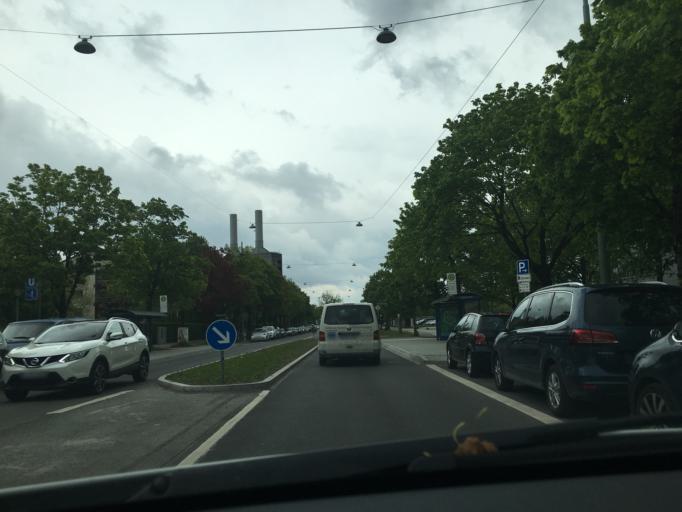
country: DE
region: Bavaria
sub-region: Upper Bavaria
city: Neuried
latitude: 48.0948
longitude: 11.5002
